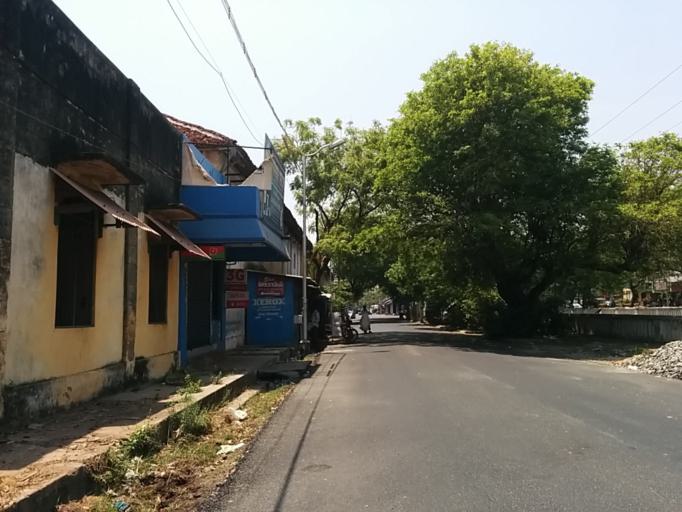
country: IN
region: Pondicherry
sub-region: Puducherry
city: Puducherry
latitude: 11.9256
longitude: 79.8312
